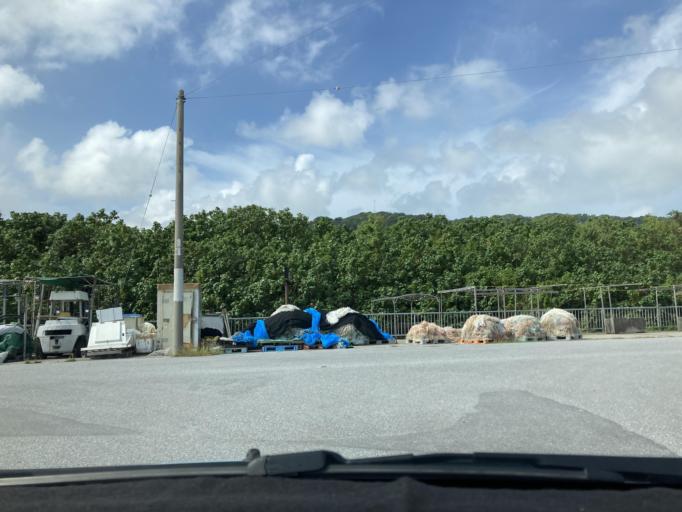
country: JP
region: Okinawa
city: Ginowan
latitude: 26.1501
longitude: 127.8071
